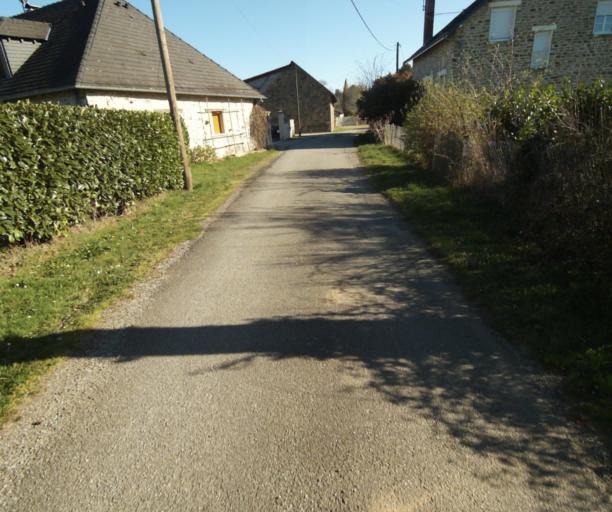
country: FR
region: Limousin
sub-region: Departement de la Correze
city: Seilhac
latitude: 45.3873
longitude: 1.7296
